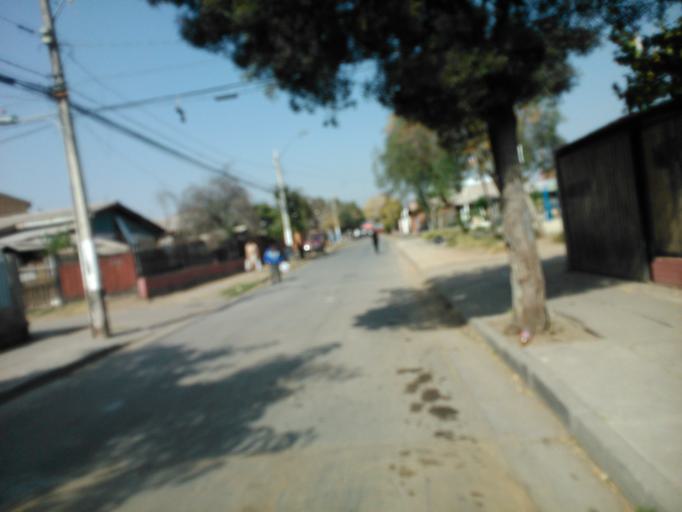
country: CL
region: Santiago Metropolitan
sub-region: Provincia de Cordillera
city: Puente Alto
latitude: -33.5581
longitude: -70.5832
